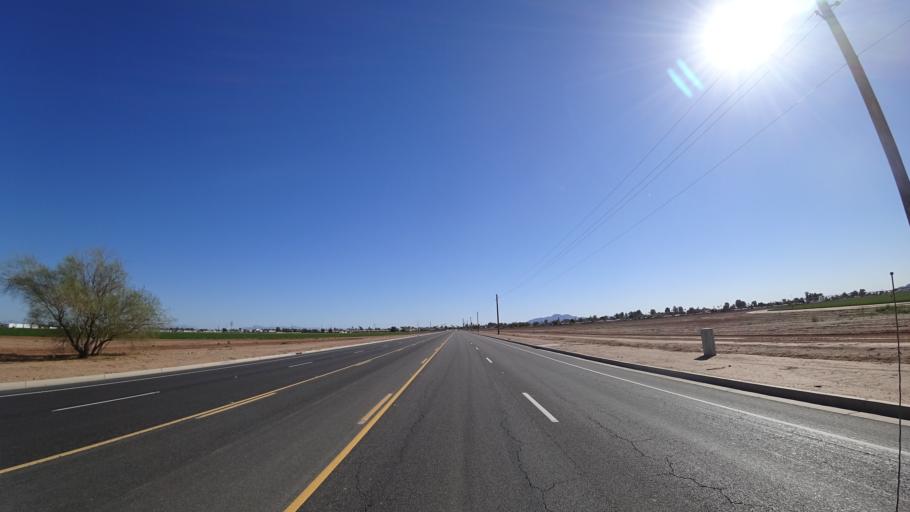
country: US
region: Arizona
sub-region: Maricopa County
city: Sun Lakes
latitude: 33.2192
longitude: -111.9001
